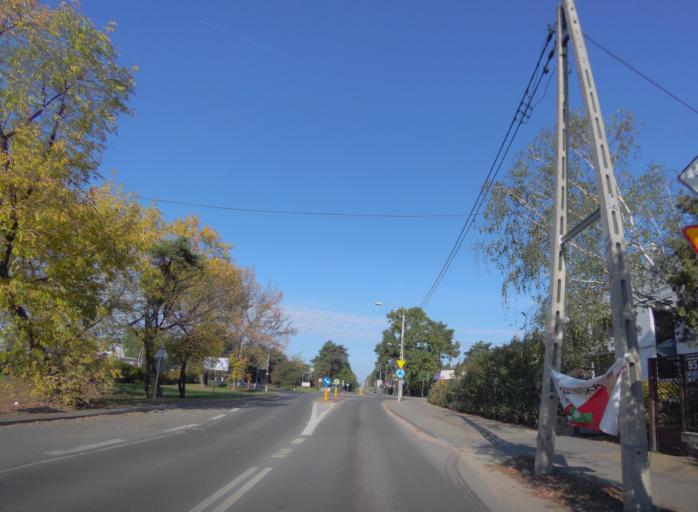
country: PL
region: Masovian Voivodeship
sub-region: Powiat otwocki
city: Jozefow
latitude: 52.1372
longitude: 21.2361
